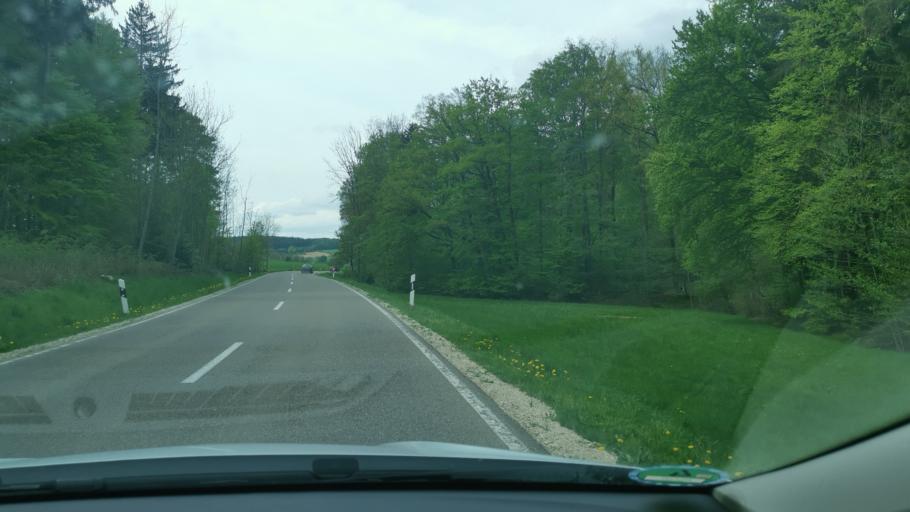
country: DE
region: Bavaria
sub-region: Swabia
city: Schiltberg
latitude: 48.4472
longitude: 11.2576
